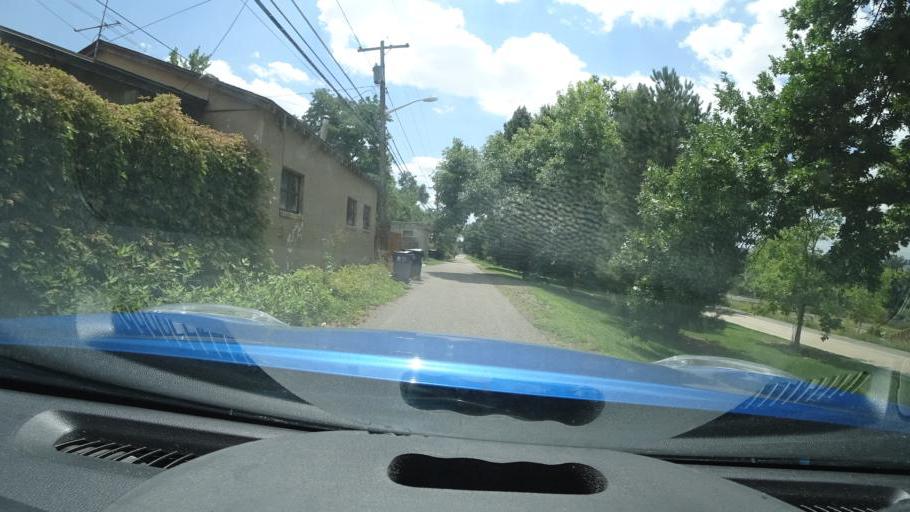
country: US
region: Colorado
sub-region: Arapahoe County
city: Englewood
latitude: 39.6759
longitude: -104.9966
